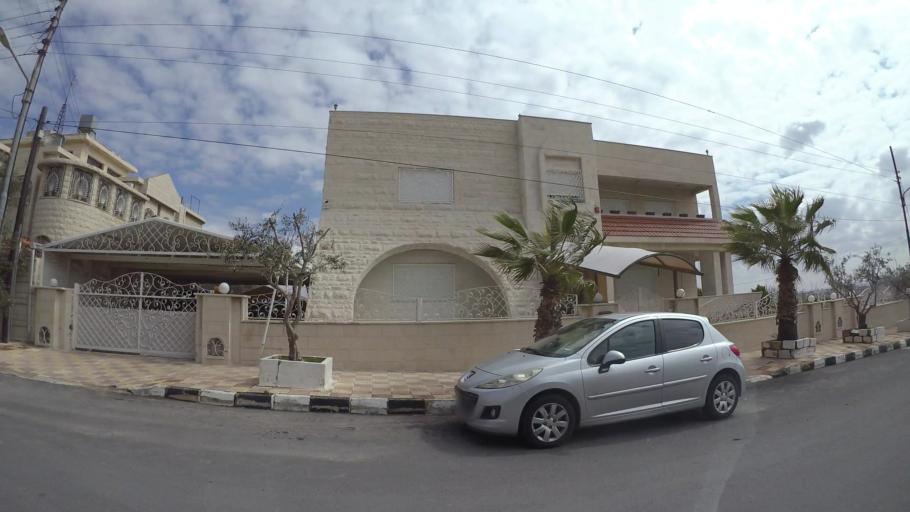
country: JO
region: Amman
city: Amman
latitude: 31.9987
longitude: 35.9172
